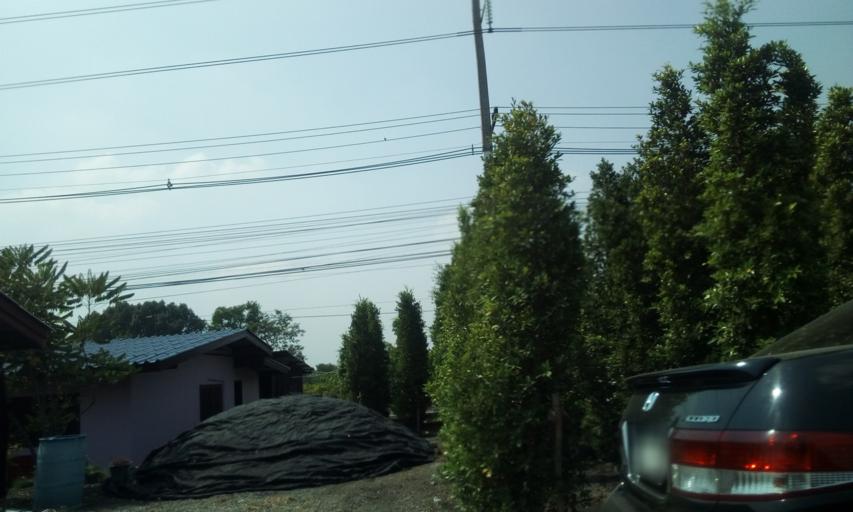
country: TH
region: Nakhon Nayok
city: Ongkharak
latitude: 14.0971
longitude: 100.9439
